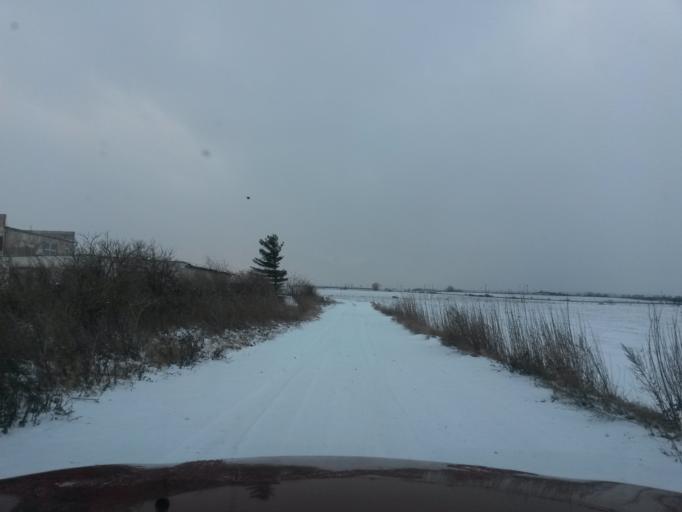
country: SK
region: Kosicky
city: Kosice
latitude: 48.6319
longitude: 21.2721
